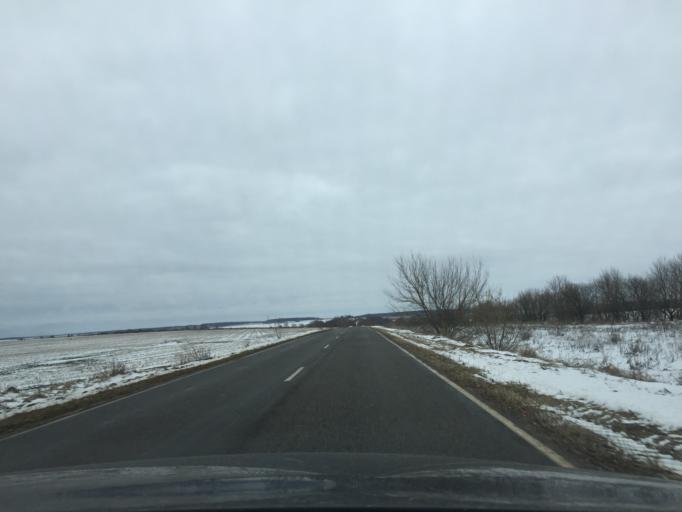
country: RU
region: Tula
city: Teploye
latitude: 53.7990
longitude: 37.5916
